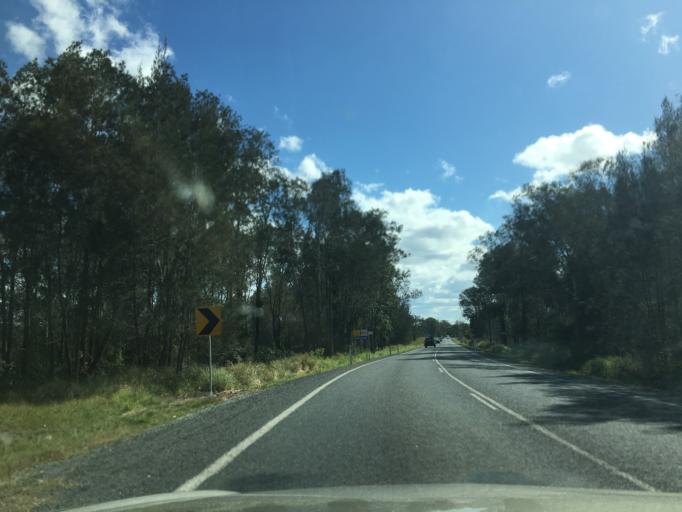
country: AU
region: Queensland
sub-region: Logan
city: Logan Reserve
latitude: -27.7525
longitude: 153.1239
